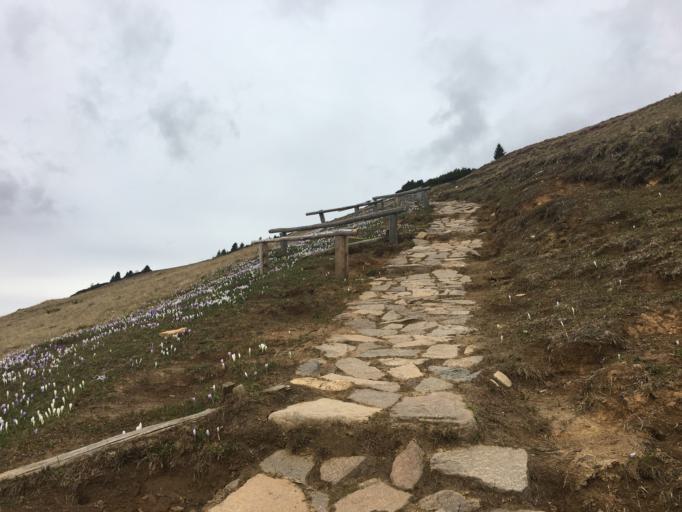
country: IT
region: Trentino-Alto Adige
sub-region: Provincia di Trento
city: Varena
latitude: 46.3486
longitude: 11.4476
